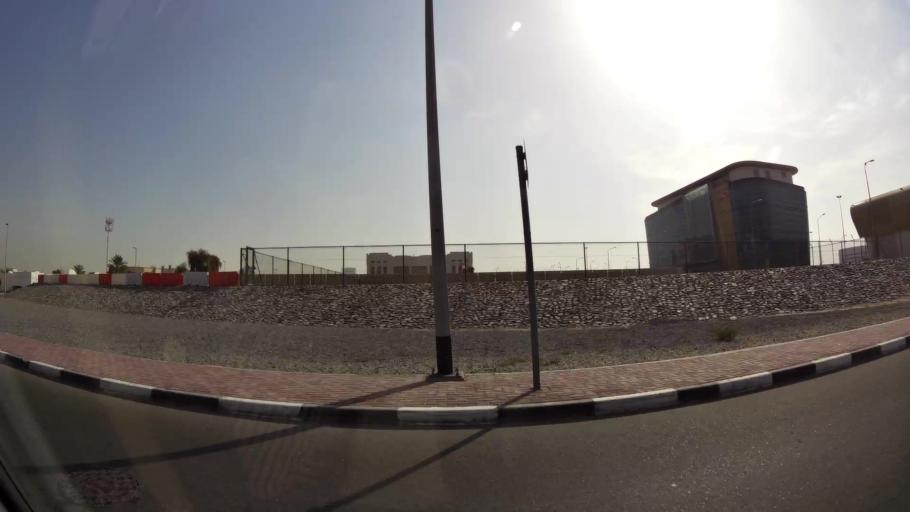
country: AE
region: Ash Shariqah
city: Sharjah
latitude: 25.2579
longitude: 55.4034
